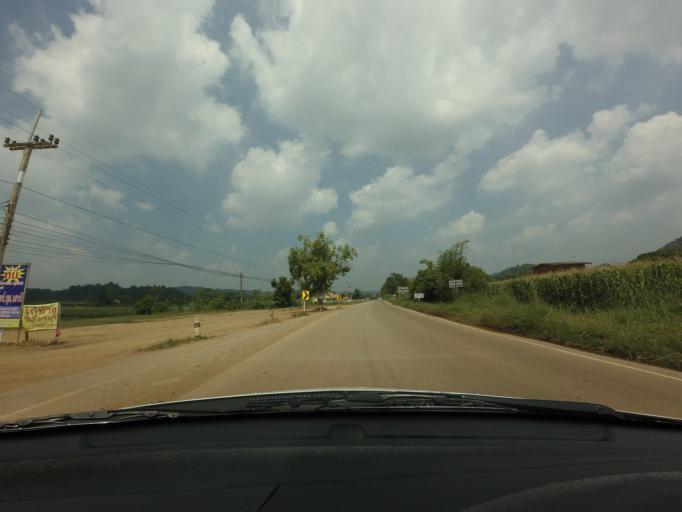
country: TH
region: Nakhon Ratchasima
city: Pak Chong
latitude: 14.5557
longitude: 101.5733
